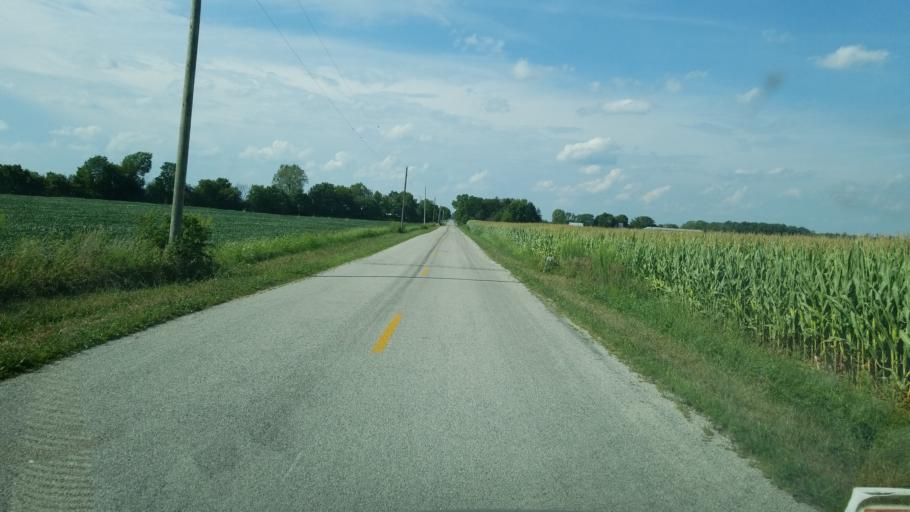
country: US
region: Ohio
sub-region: Union County
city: Richwood
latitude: 40.5193
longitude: -83.2822
